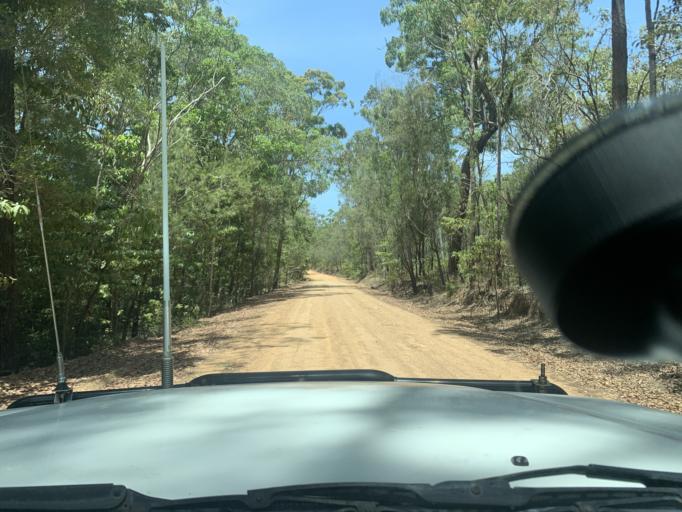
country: AU
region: Queensland
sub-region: Cairns
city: Redlynch
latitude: -16.9260
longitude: 145.6034
